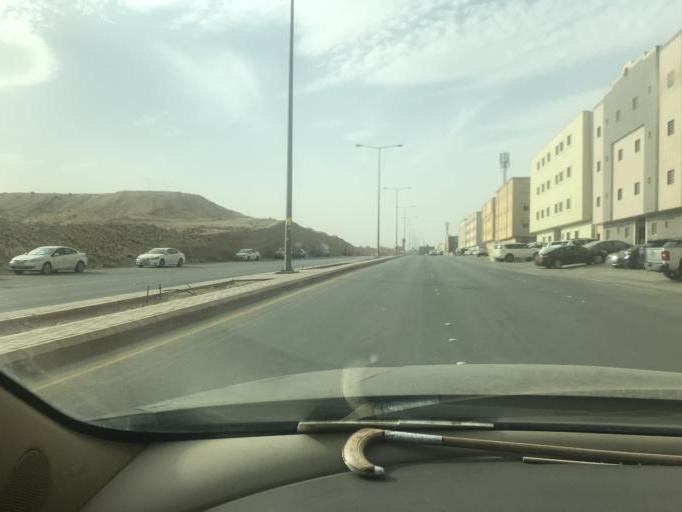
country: SA
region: Ar Riyad
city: Riyadh
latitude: 24.7930
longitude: 46.6690
